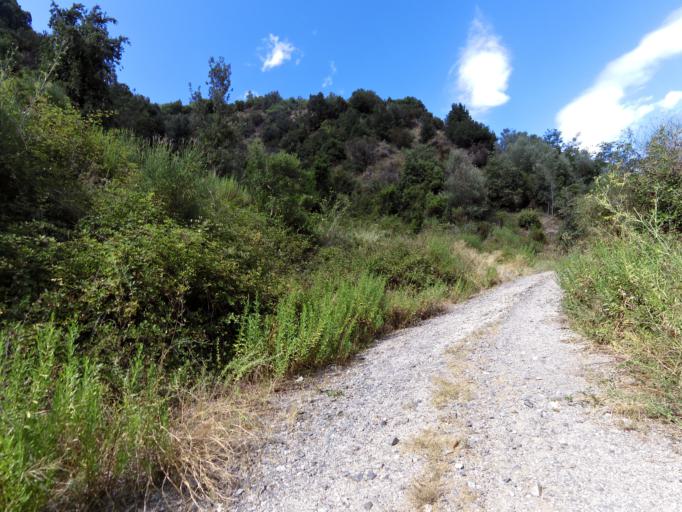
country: IT
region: Calabria
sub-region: Provincia di Reggio Calabria
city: Pazzano
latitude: 38.4732
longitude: 16.4225
